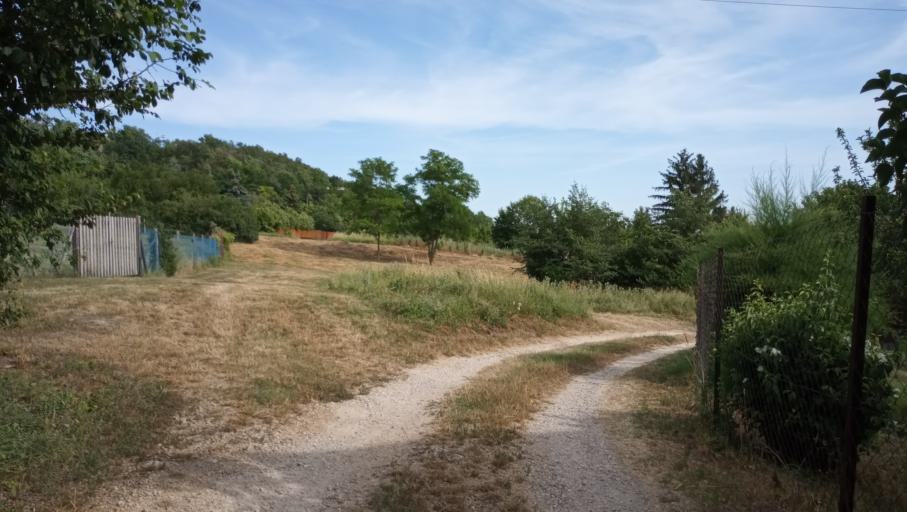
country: HU
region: Veszprem
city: Balatonkenese
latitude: 47.0400
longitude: 18.0878
